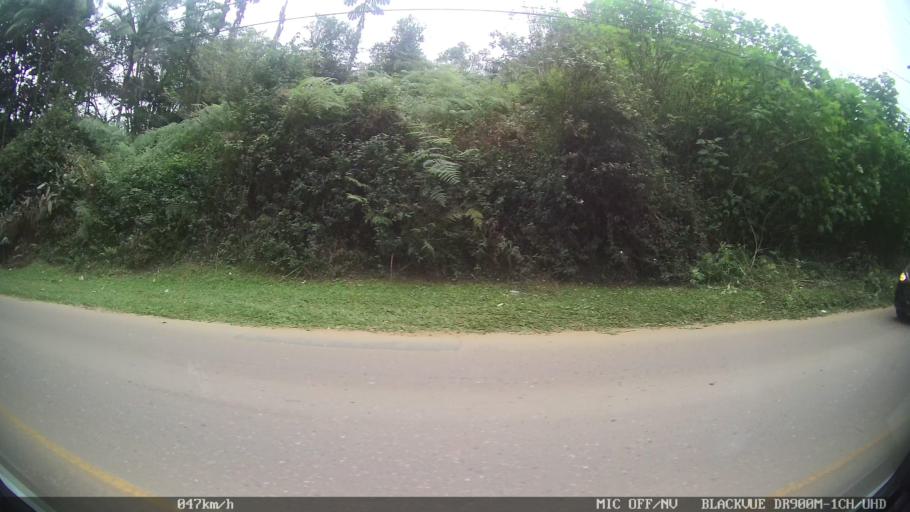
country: BR
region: Santa Catarina
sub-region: Joinville
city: Joinville
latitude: -26.3612
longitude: -48.8478
